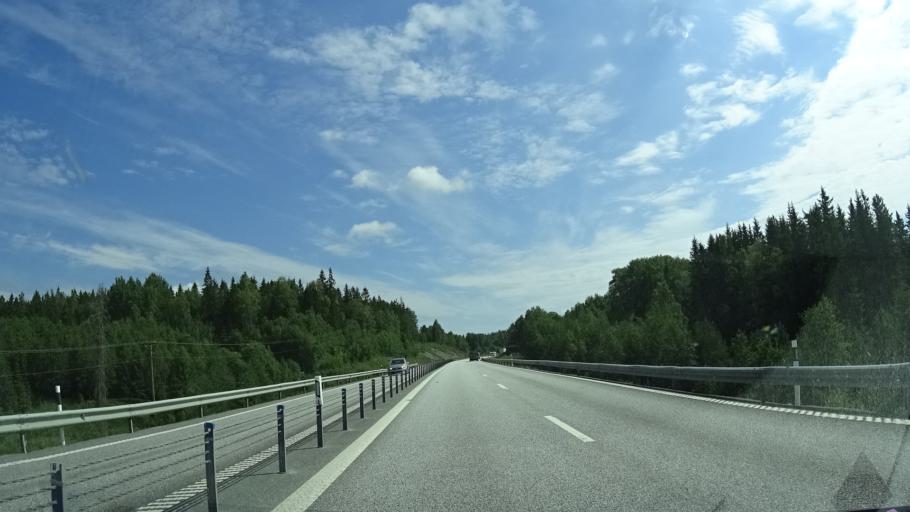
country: SE
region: OErebro
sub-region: Degerfors Kommun
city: Degerfors
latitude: 59.3242
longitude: 14.3746
